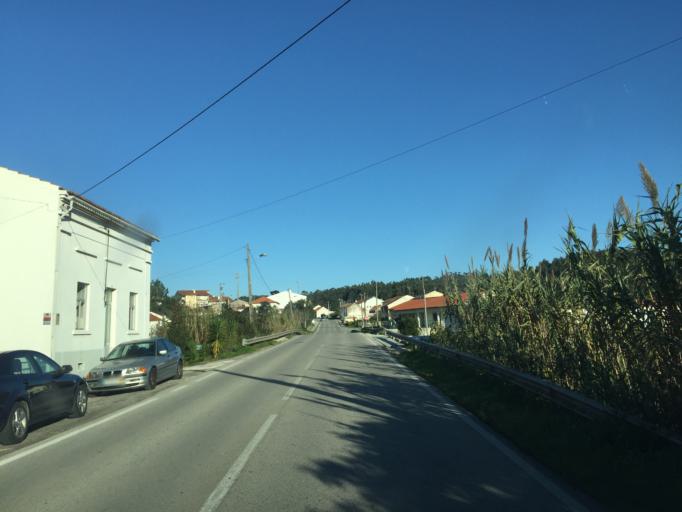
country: PT
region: Coimbra
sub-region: Figueira da Foz
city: Alhadas
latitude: 40.1639
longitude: -8.8127
